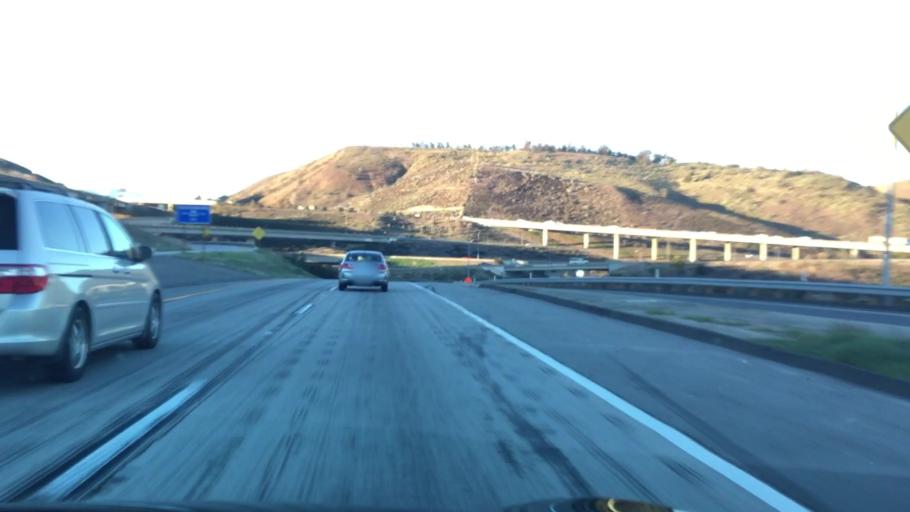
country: US
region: California
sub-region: Los Angeles County
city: Diamond Bar
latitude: 34.0625
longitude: -117.8049
